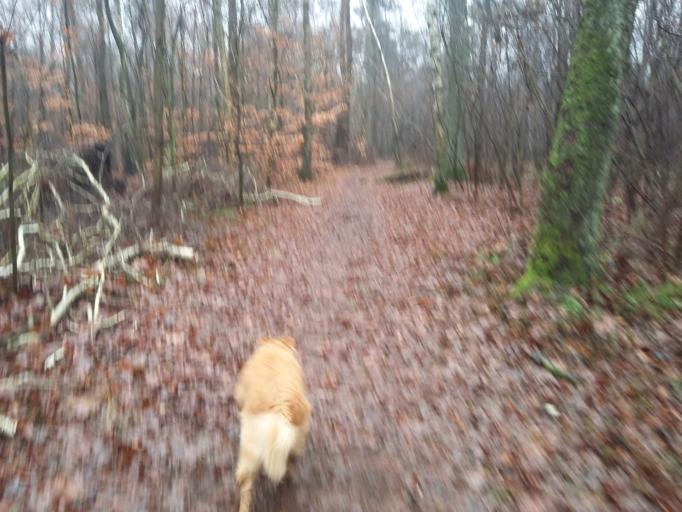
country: PL
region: Lodz Voivodeship
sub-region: Powiat pabianicki
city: Ksawerow
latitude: 51.7255
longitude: 19.3751
